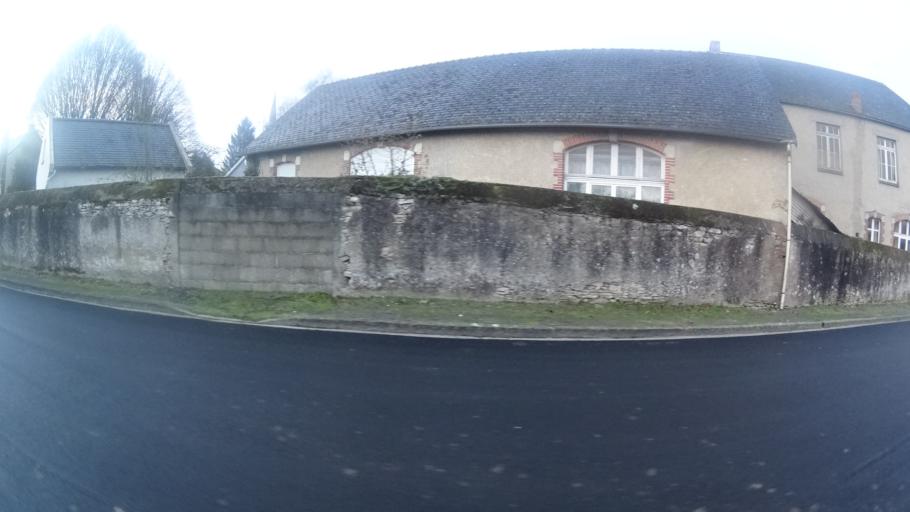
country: FR
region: Pays de la Loire
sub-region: Departement de la Loire-Atlantique
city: Saint-Nicolas-de-Redon
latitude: 47.6455
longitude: -2.0687
